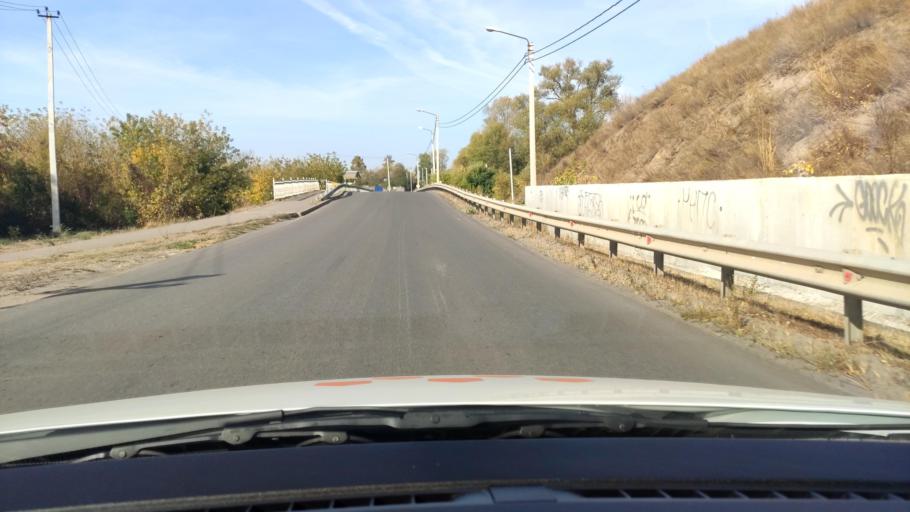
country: RU
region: Voronezj
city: Pridonskoy
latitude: 51.6642
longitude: 39.0890
